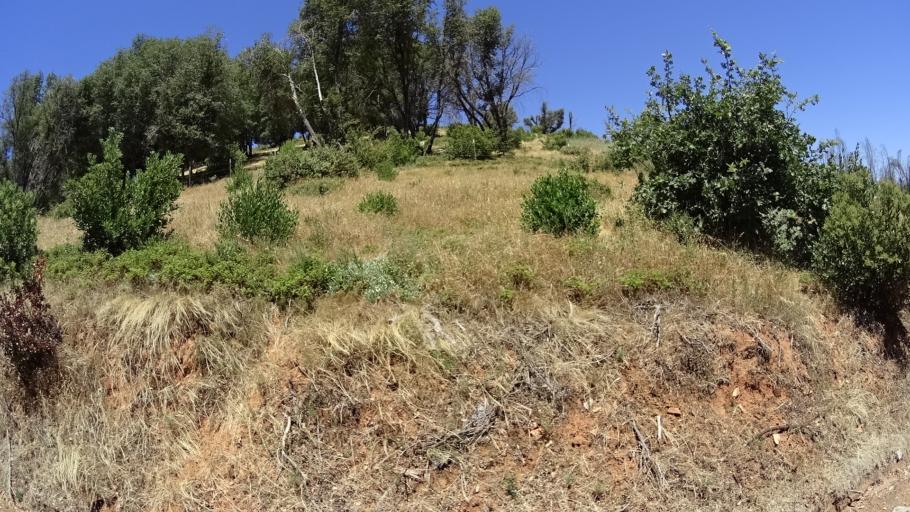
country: US
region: California
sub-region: Calaveras County
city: Mountain Ranch
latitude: 38.2360
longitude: -120.6078
